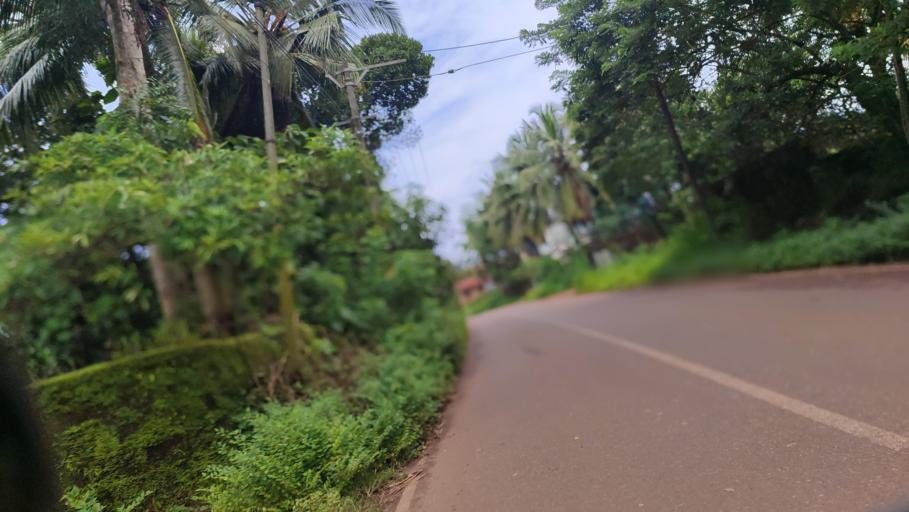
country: IN
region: Kerala
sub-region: Kasaragod District
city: Kannangad
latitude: 12.3939
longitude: 75.0535
